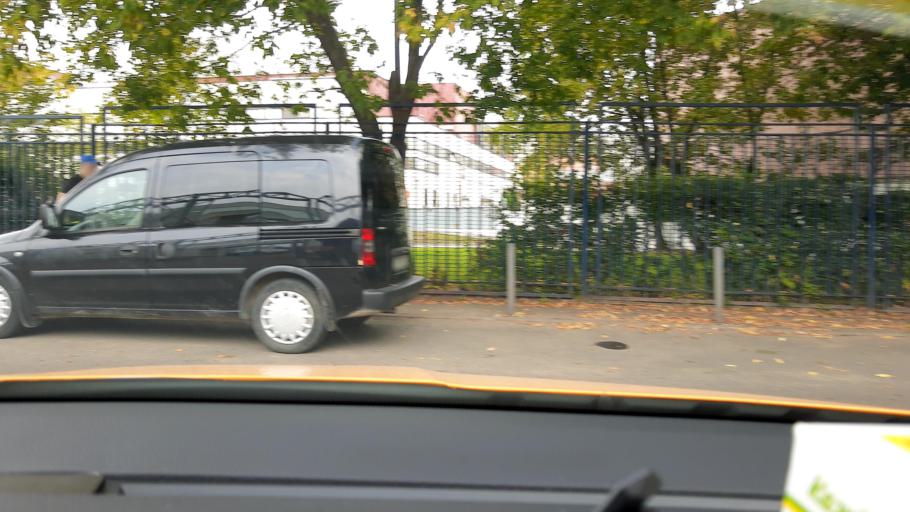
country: RU
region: Moskovskaya
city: Dorogomilovo
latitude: 55.7405
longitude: 37.5649
